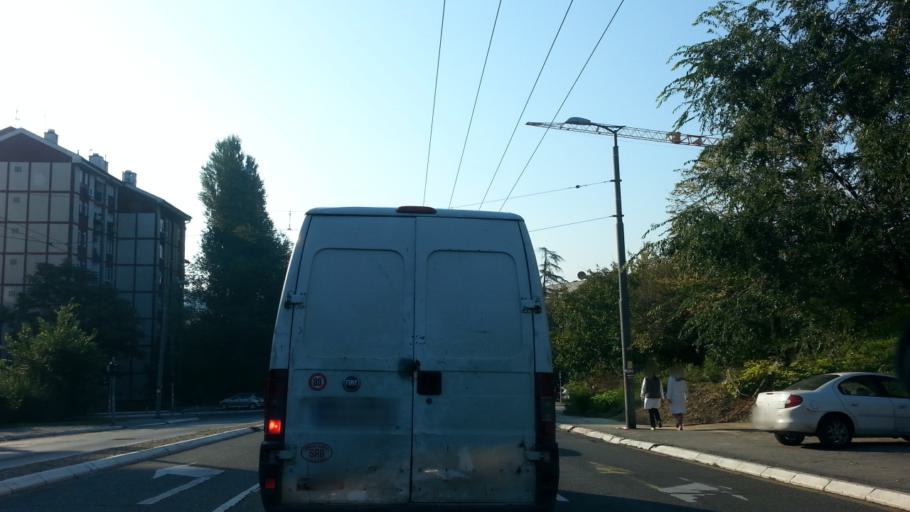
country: RS
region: Central Serbia
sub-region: Belgrade
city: Vracar
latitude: 44.7887
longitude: 20.4993
